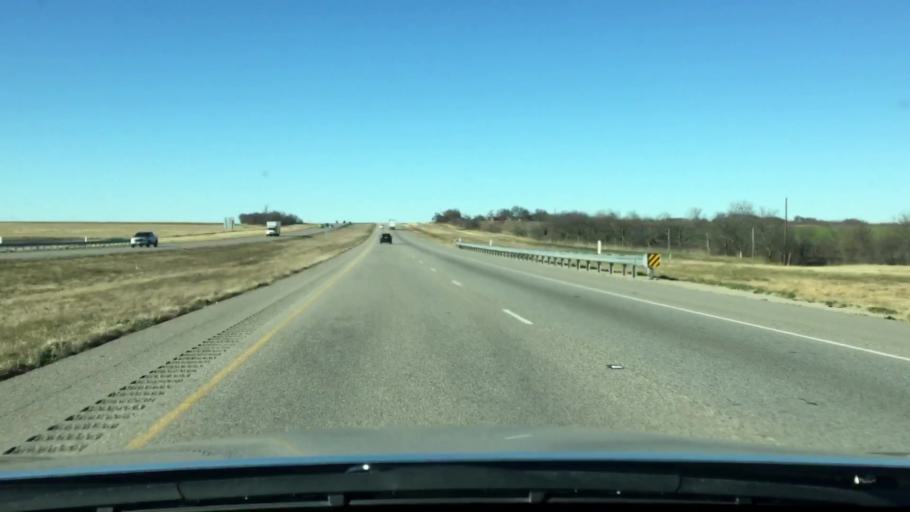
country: US
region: Texas
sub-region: Hill County
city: Itasca
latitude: 32.1139
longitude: -97.1141
